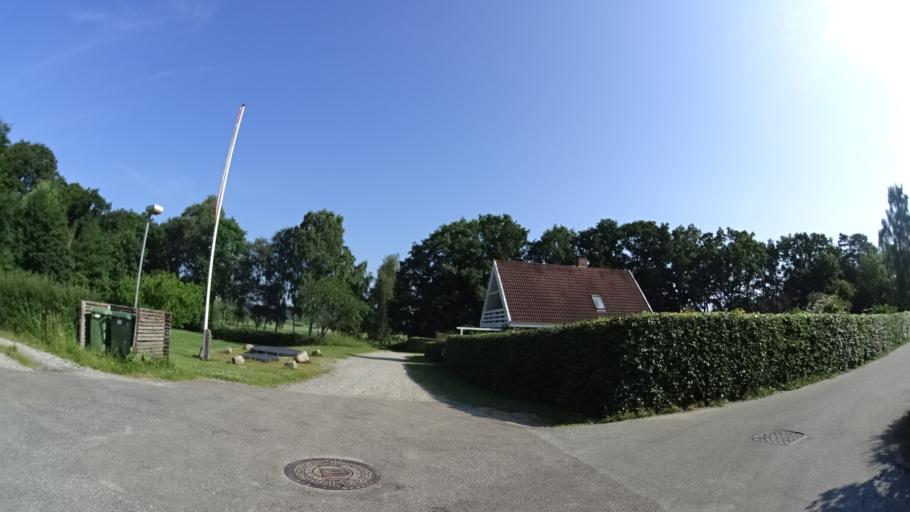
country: DK
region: Central Jutland
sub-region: Arhus Kommune
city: Stavtrup
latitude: 56.1402
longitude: 10.1203
